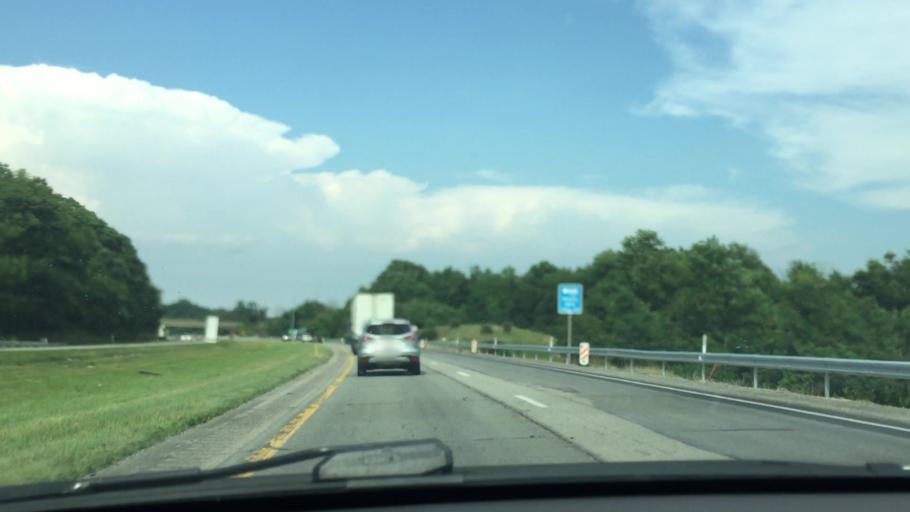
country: US
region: West Virginia
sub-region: Ohio County
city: West Liberty
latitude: 40.0977
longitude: -80.5108
